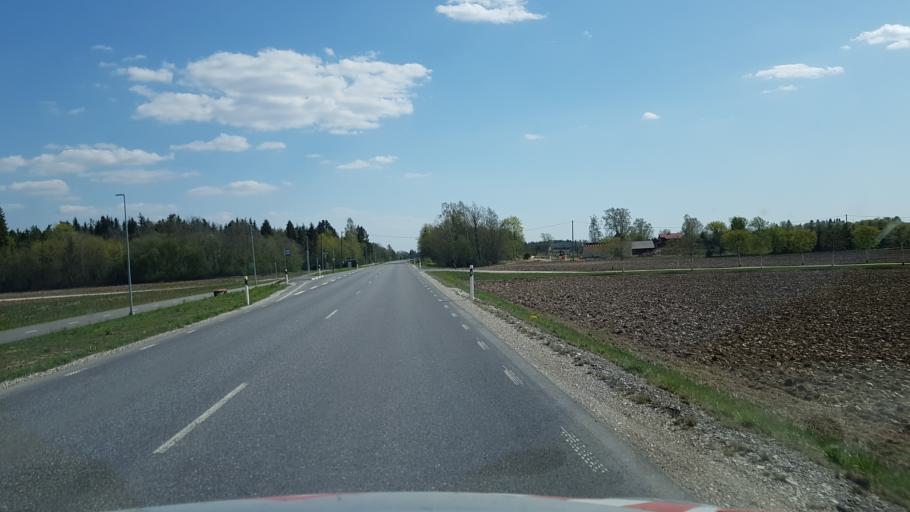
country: EE
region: Harju
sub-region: Rae vald
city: Vaida
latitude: 59.1918
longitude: 25.1114
